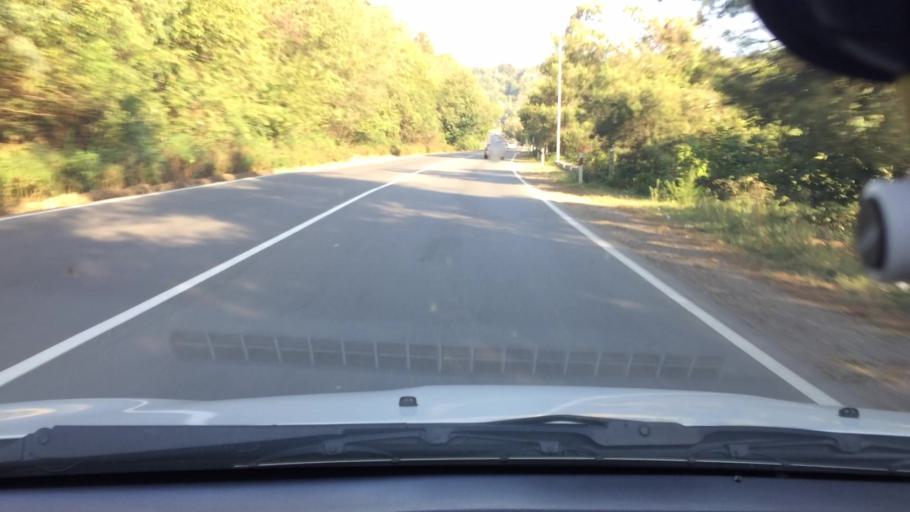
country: GE
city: Shorapani
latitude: 42.0947
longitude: 43.0770
